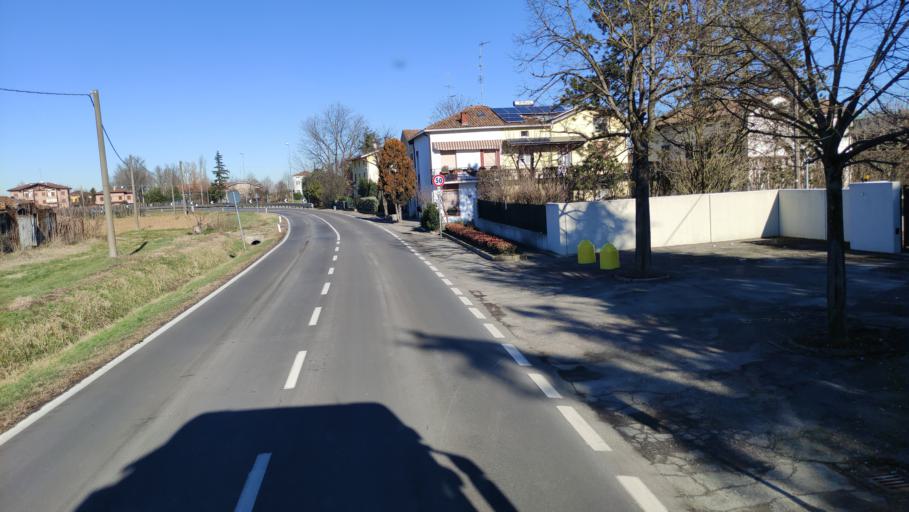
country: IT
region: Emilia-Romagna
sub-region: Provincia di Reggio Emilia
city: Rio Saliceto
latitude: 44.8057
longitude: 10.7831
